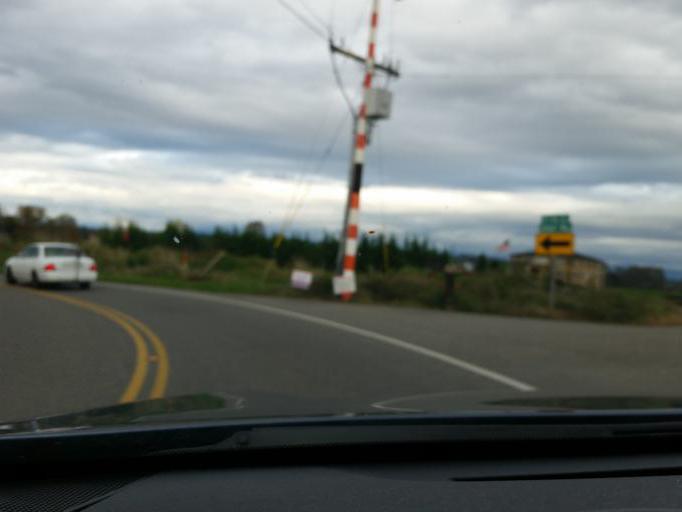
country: US
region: Washington
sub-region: Snohomish County
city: Snohomish
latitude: 47.9014
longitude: -122.0993
